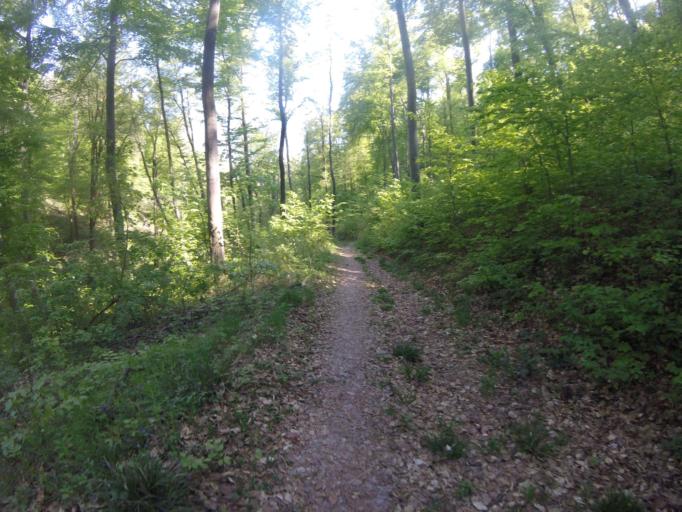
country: HU
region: Pest
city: Pilisszentkereszt
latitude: 47.7101
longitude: 18.8933
